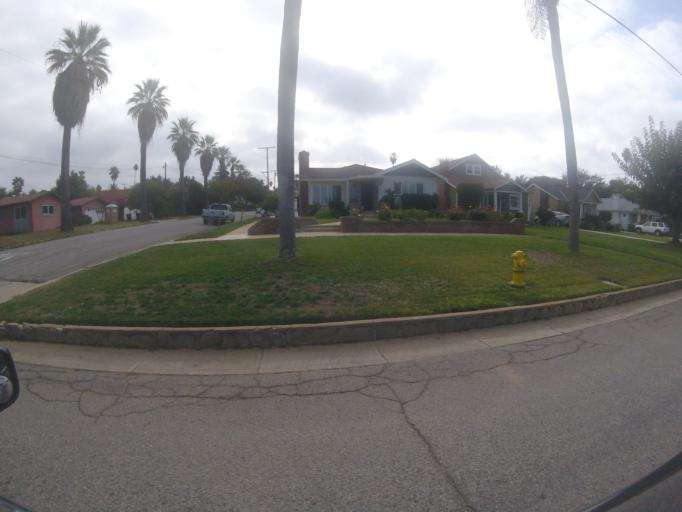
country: US
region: California
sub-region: San Bernardino County
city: Redlands
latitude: 34.0393
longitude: -117.1833
